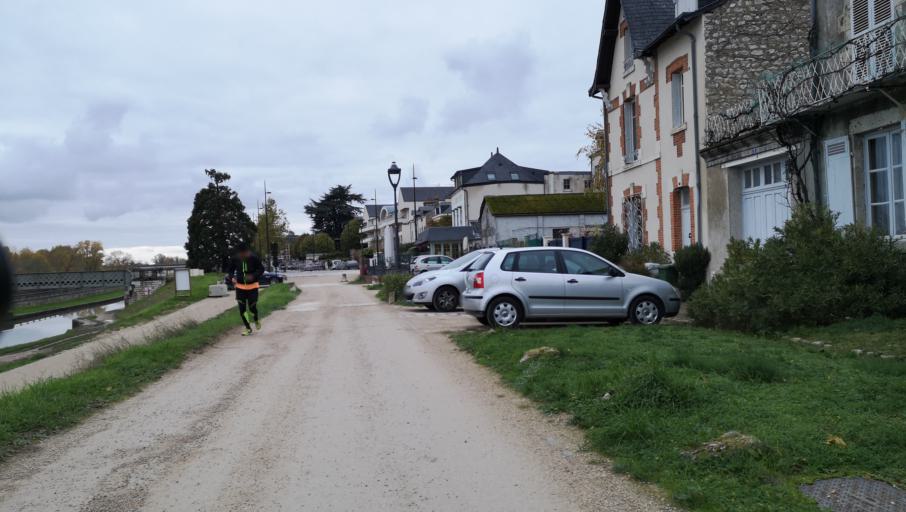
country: FR
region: Centre
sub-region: Departement du Loiret
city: Saint-Jean-le-Blanc
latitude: 47.9007
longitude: 1.9319
